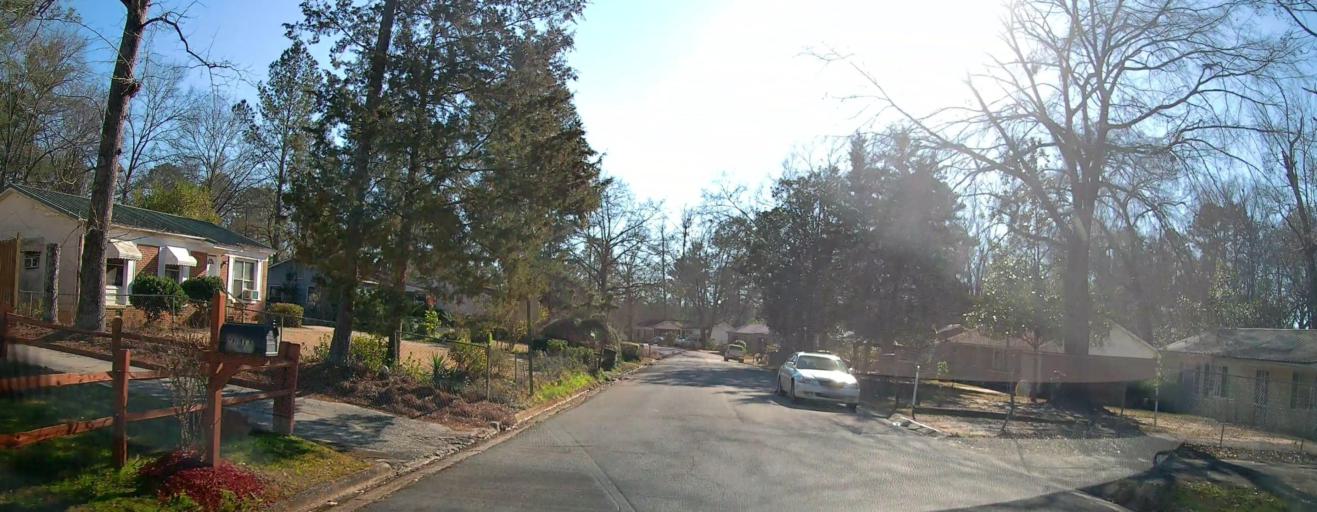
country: US
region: Georgia
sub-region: Sumter County
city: Americus
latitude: 32.0781
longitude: -84.2490
